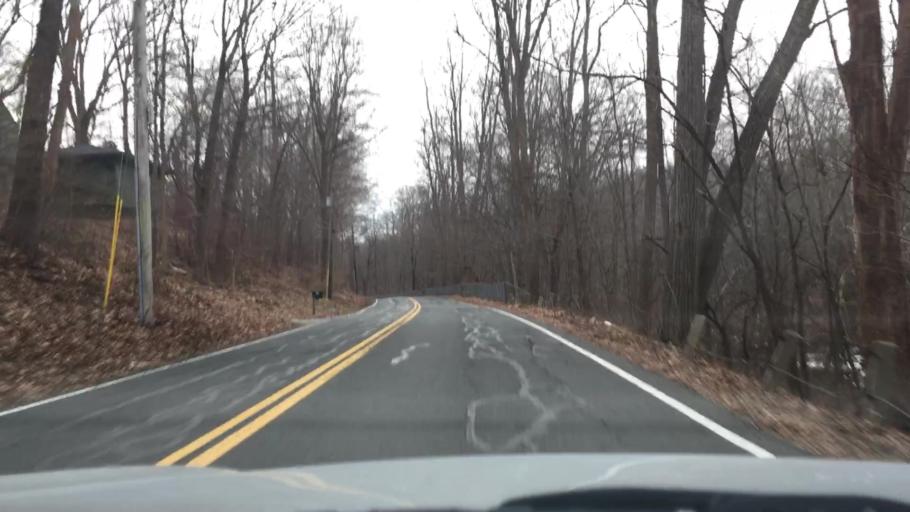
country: US
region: Massachusetts
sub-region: Hampshire County
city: Northampton
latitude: 42.3235
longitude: -72.6672
